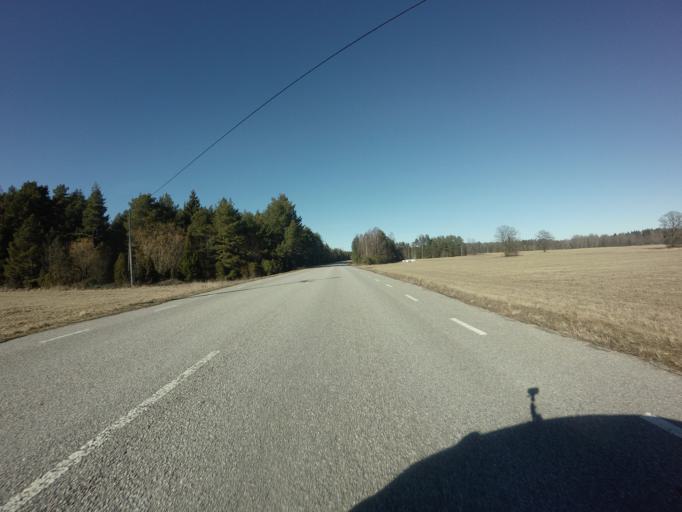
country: EE
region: Saare
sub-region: Kuressaare linn
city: Kuressaare
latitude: 58.4781
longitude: 22.2313
